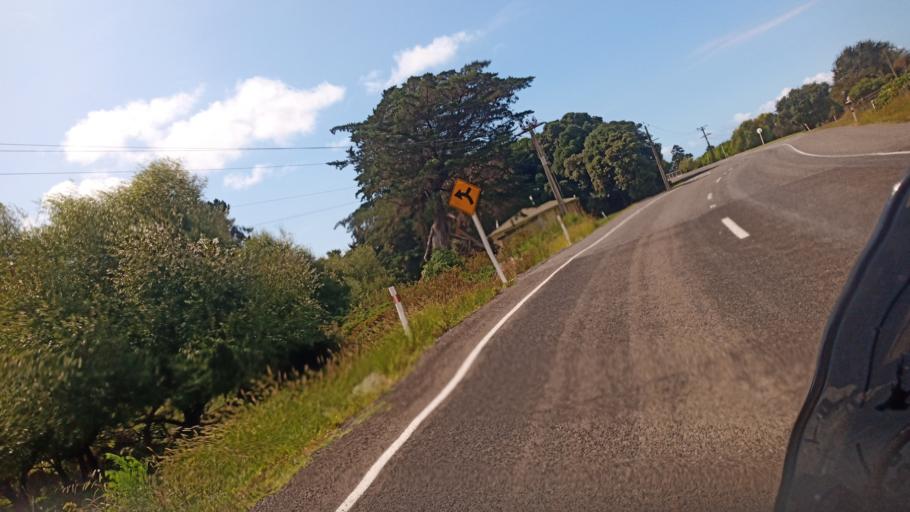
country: NZ
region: Gisborne
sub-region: Gisborne District
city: Gisborne
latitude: -38.1319
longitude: 178.3108
